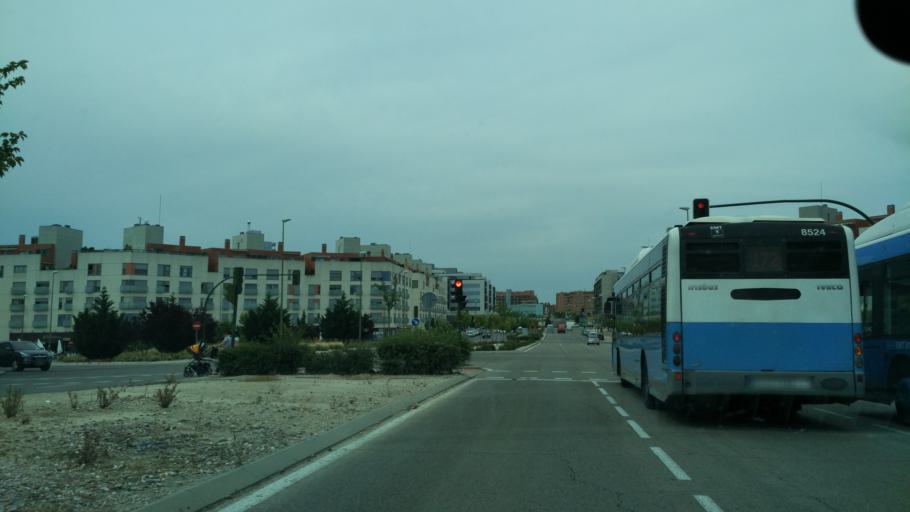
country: ES
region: Madrid
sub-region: Provincia de Madrid
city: Las Tablas
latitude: 40.5107
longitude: -3.6675
